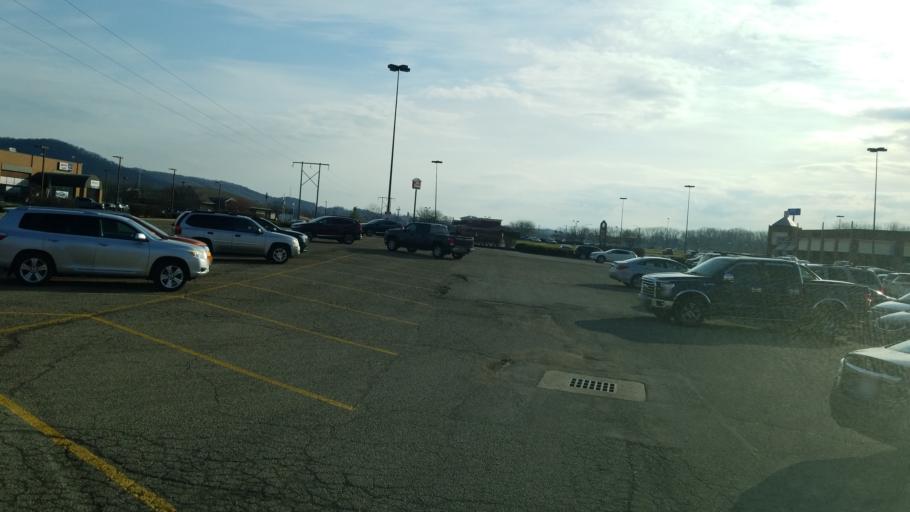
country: US
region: Ohio
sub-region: Ross County
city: Chillicothe
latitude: 39.3470
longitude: -82.9803
